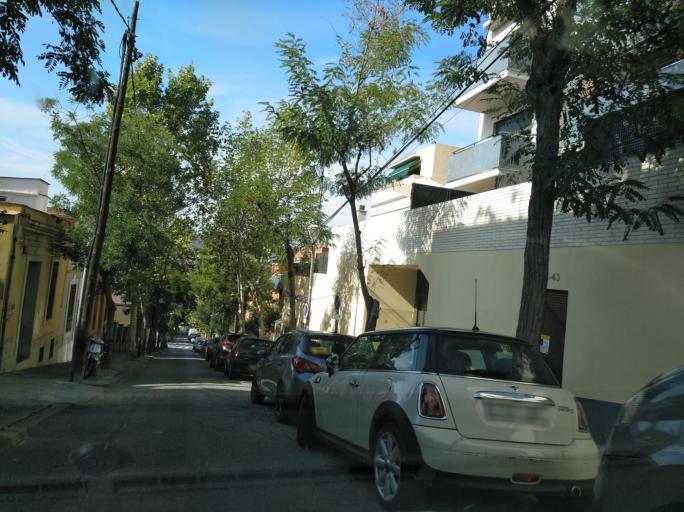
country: ES
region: Catalonia
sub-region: Provincia de Barcelona
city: Horta-Guinardo
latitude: 41.4231
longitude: 2.1620
